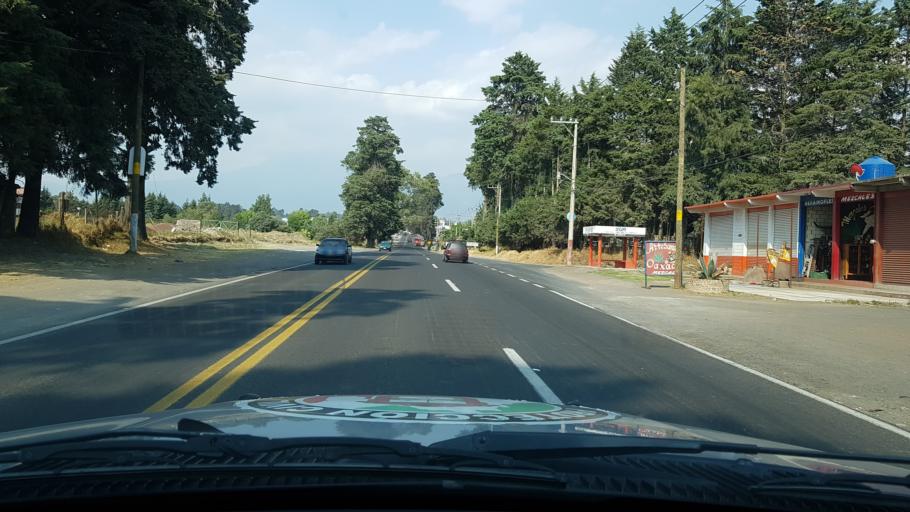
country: MX
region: Mexico
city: Ozumba de Alzate
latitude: 19.0426
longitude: -98.8004
